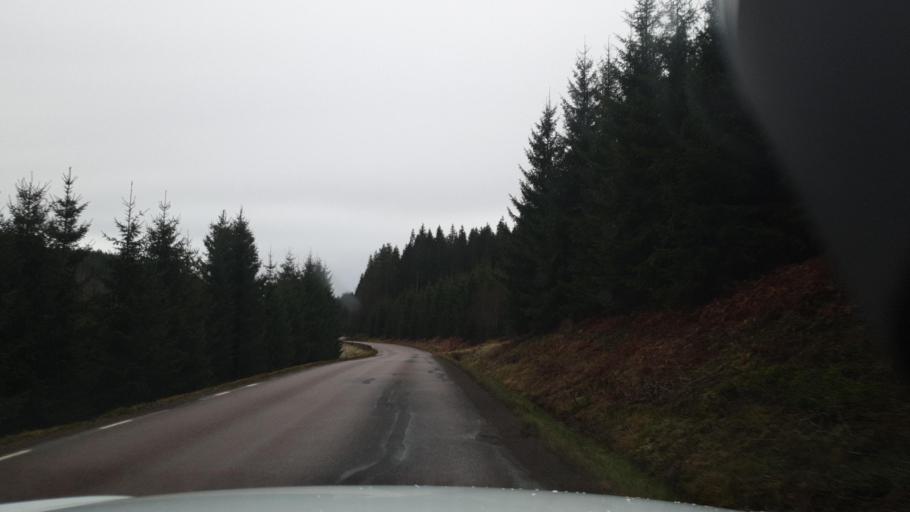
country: SE
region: Vaermland
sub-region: Arvika Kommun
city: Arvika
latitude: 59.7052
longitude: 12.7916
